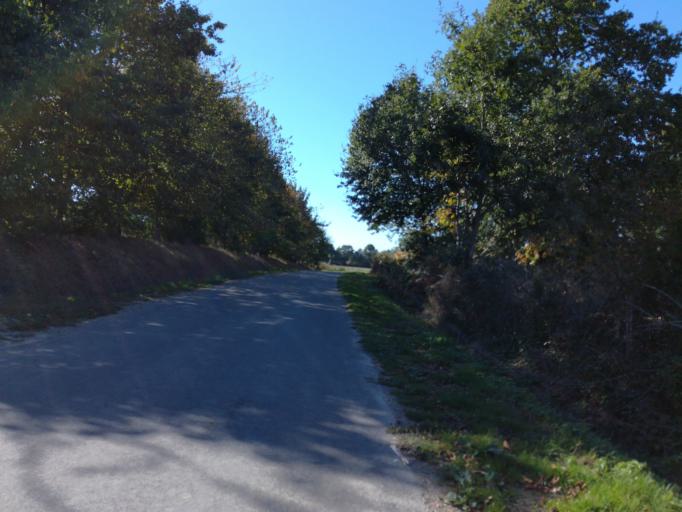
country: FR
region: Brittany
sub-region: Departement d'Ille-et-Vilaine
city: Saint-Jean-sur-Couesnon
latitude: 48.2612
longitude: -1.3673
